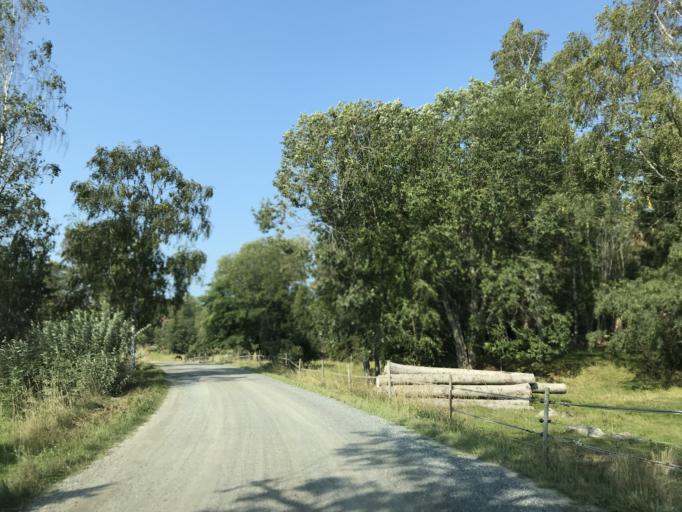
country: SE
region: Stockholm
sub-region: Norrtalje Kommun
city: Bjorko
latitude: 59.8490
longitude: 19.0143
